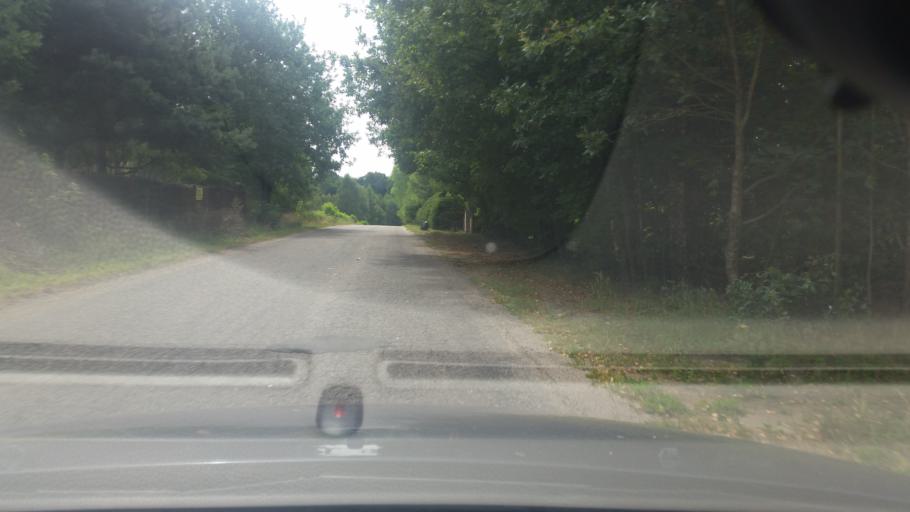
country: PL
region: Pomeranian Voivodeship
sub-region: Powiat wejherowski
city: Choczewo
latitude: 54.7642
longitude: 17.7928
